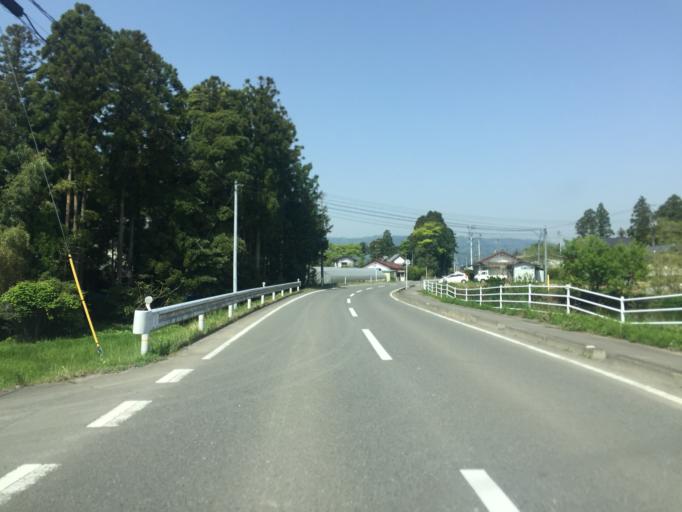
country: JP
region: Miyagi
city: Marumori
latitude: 37.7723
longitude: 140.9274
